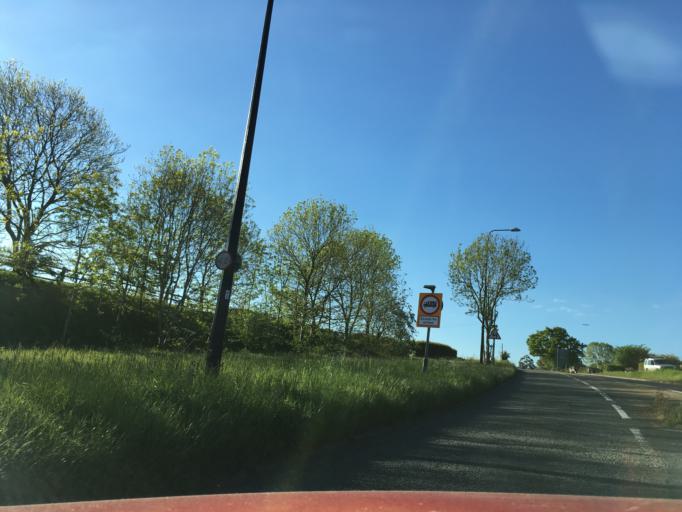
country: GB
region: England
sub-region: North Somerset
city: Long Ashton
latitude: 51.4195
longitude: -2.6905
